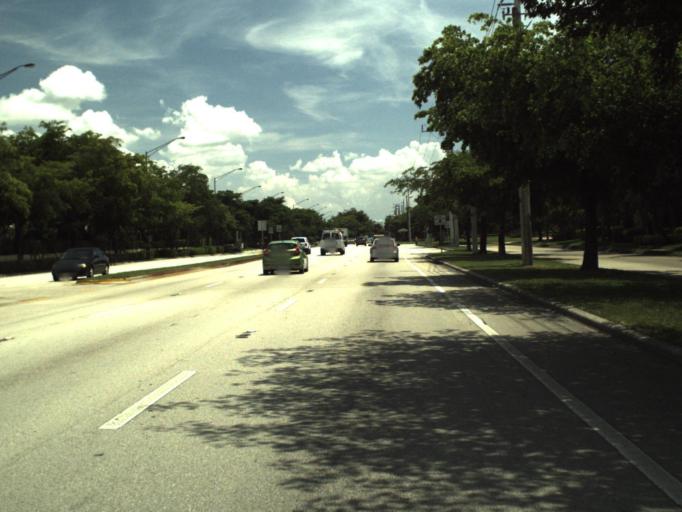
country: US
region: Florida
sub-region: Broward County
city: Plantation
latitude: 26.1397
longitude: -80.2570
